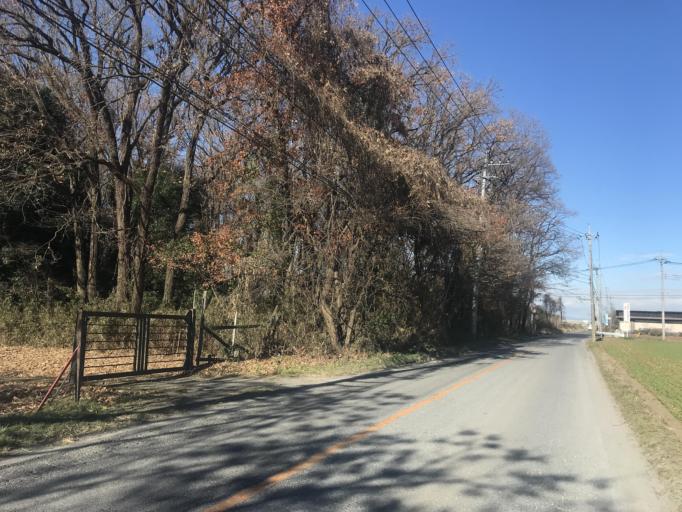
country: JP
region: Ibaraki
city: Yuki
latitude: 36.3565
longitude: 139.8768
